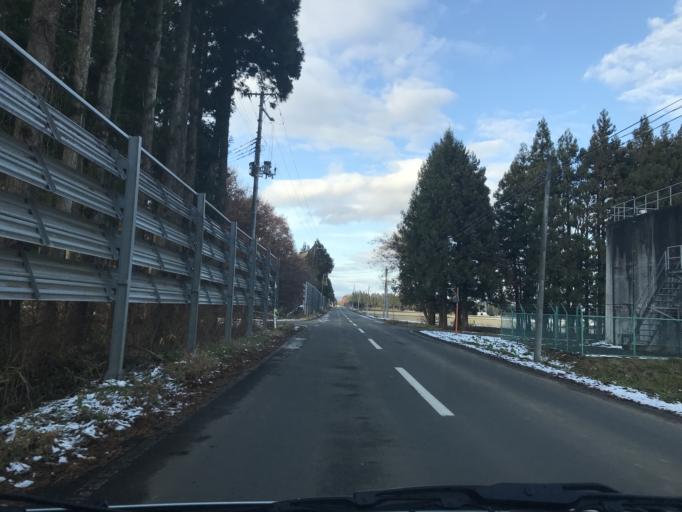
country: JP
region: Iwate
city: Kitakami
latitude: 39.2465
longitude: 141.0326
